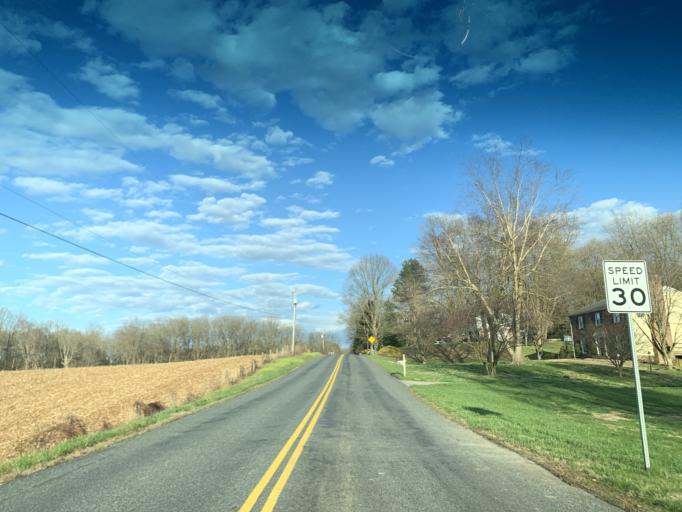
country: US
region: Maryland
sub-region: Harford County
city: South Bel Air
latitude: 39.5957
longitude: -76.2679
